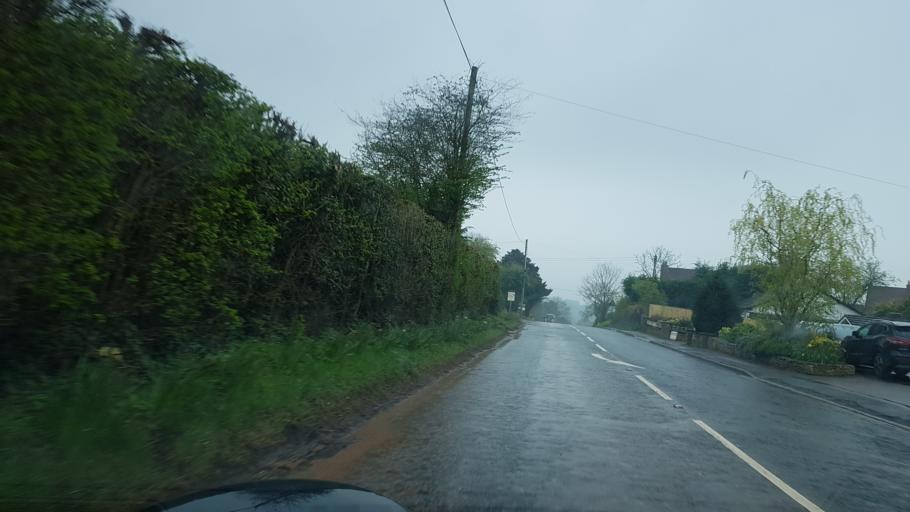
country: GB
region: England
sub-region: Herefordshire
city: Moreton Jeffries
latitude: 52.1490
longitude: -2.5512
